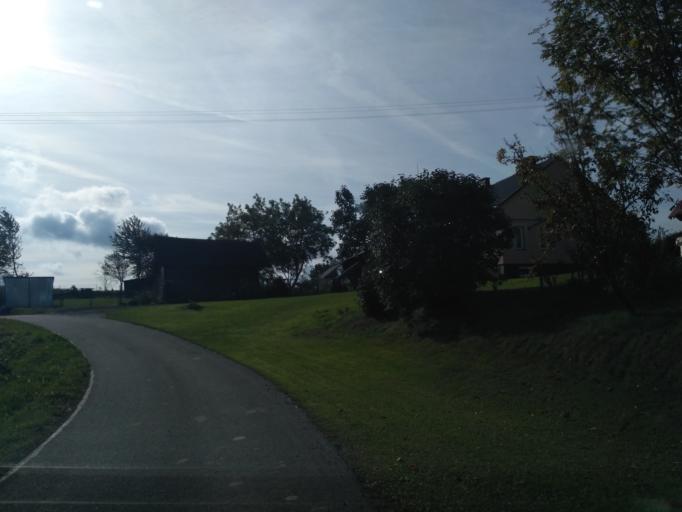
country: PL
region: Subcarpathian Voivodeship
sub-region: Powiat strzyzowski
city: Strzyzow
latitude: 49.8487
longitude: 21.8310
